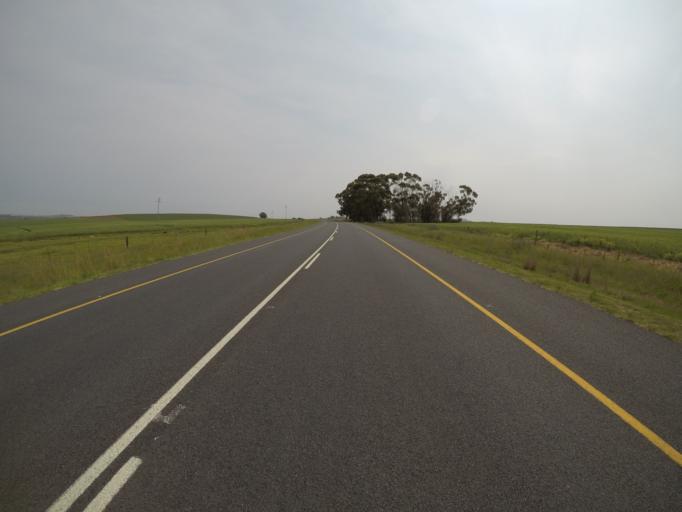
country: ZA
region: Western Cape
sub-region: West Coast District Municipality
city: Malmesbury
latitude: -33.5124
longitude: 18.8452
